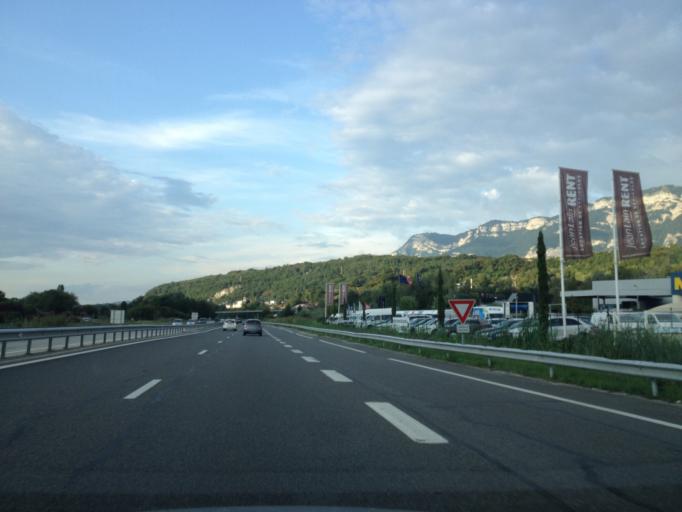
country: FR
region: Rhone-Alpes
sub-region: Departement de la Savoie
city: Voglans
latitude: 45.6212
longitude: 5.8875
